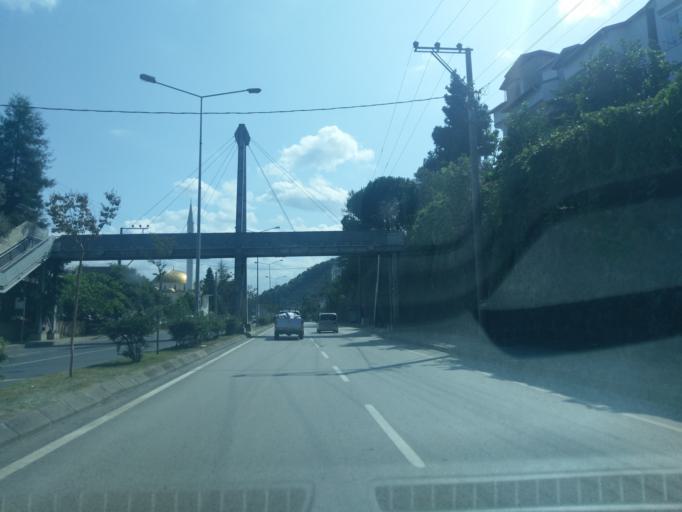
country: TR
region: Ordu
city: Ordu
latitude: 41.0047
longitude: 37.8701
